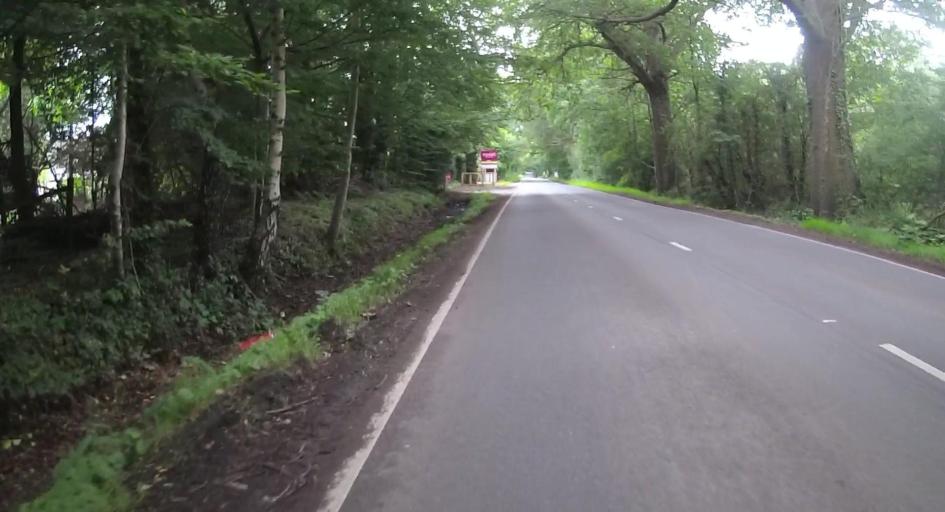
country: GB
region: England
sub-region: Wokingham
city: Wokingham
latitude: 51.3909
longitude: -0.8173
